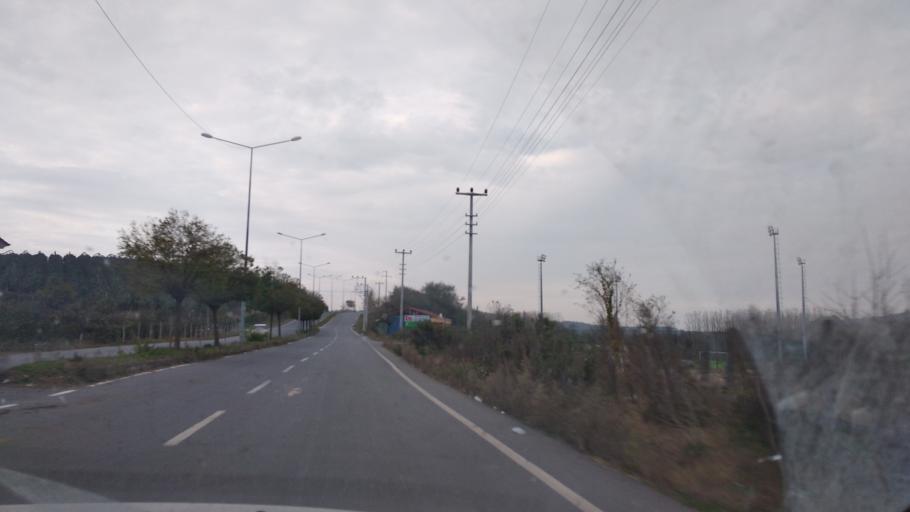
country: TR
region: Sakarya
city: Ortakoy
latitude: 41.0424
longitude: 30.6401
